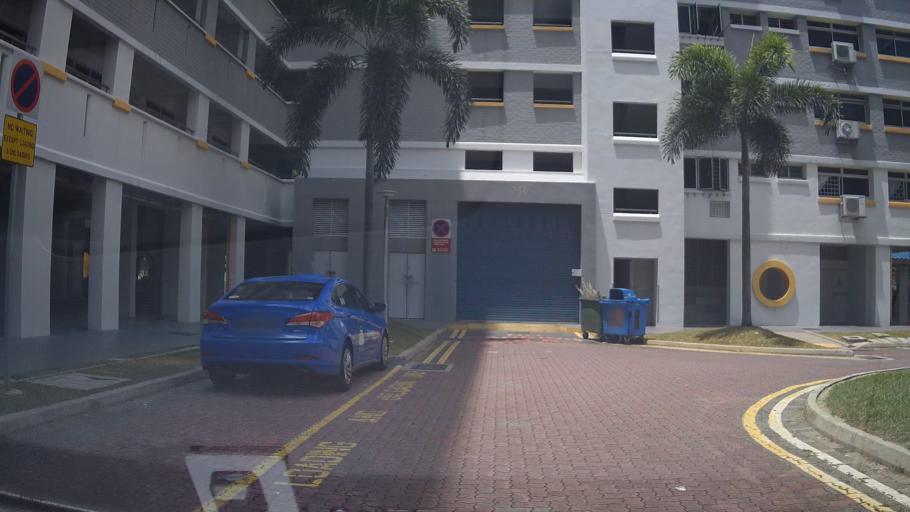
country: MY
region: Johor
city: Kampung Pasir Gudang Baru
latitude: 1.3764
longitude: 103.9331
